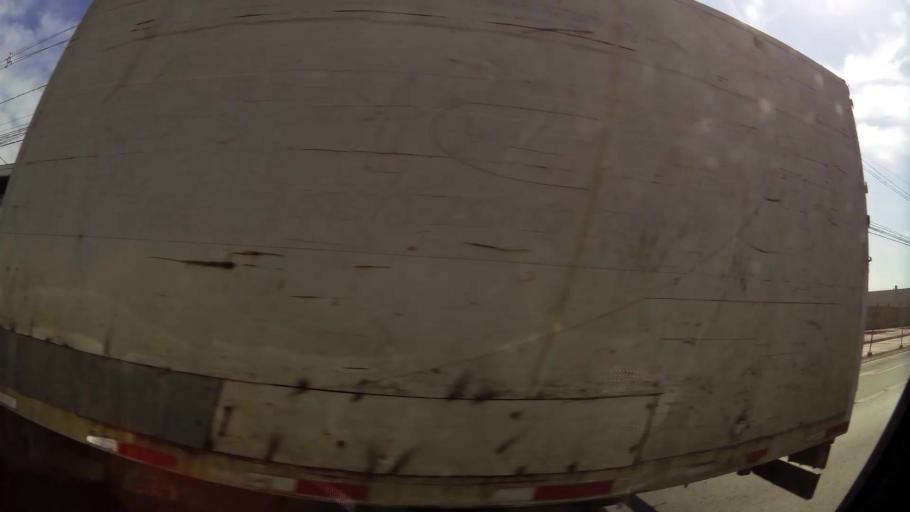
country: CL
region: Santiago Metropolitan
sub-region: Provincia de Talagante
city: Talagante
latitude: -33.6707
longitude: -70.9420
